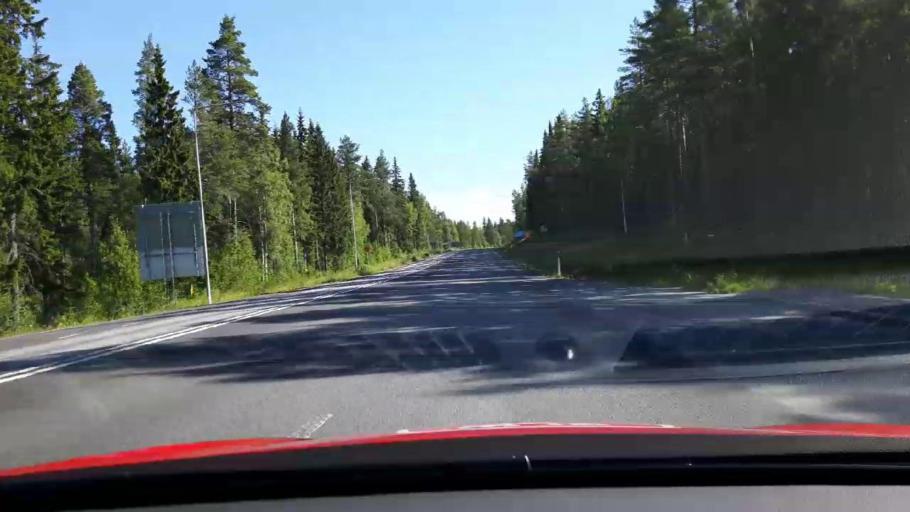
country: SE
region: Jaemtland
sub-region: OEstersunds Kommun
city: Ostersund
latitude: 63.2044
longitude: 14.6801
